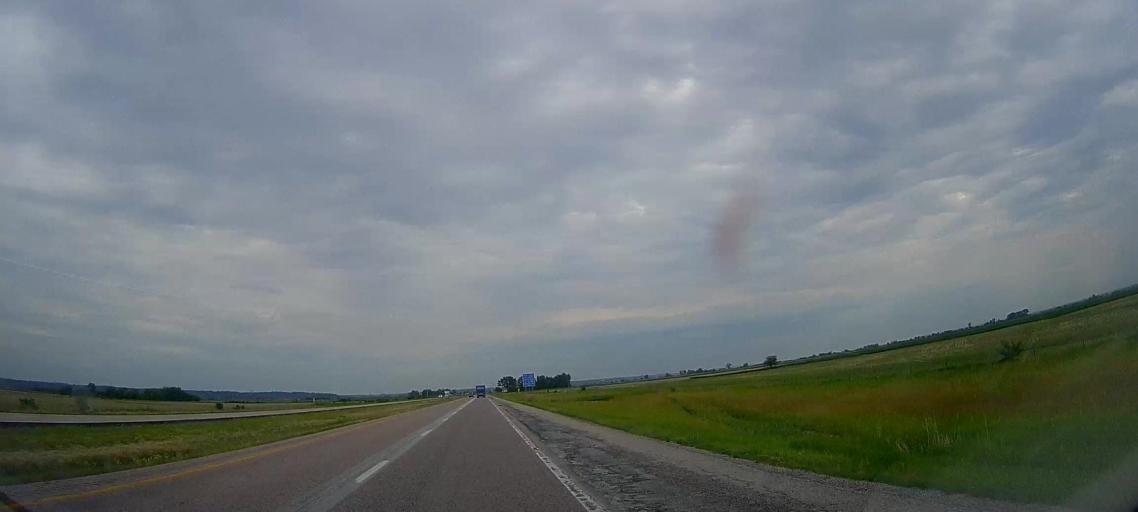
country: US
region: Iowa
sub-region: Harrison County
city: Missouri Valley
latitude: 41.5994
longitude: -95.9610
